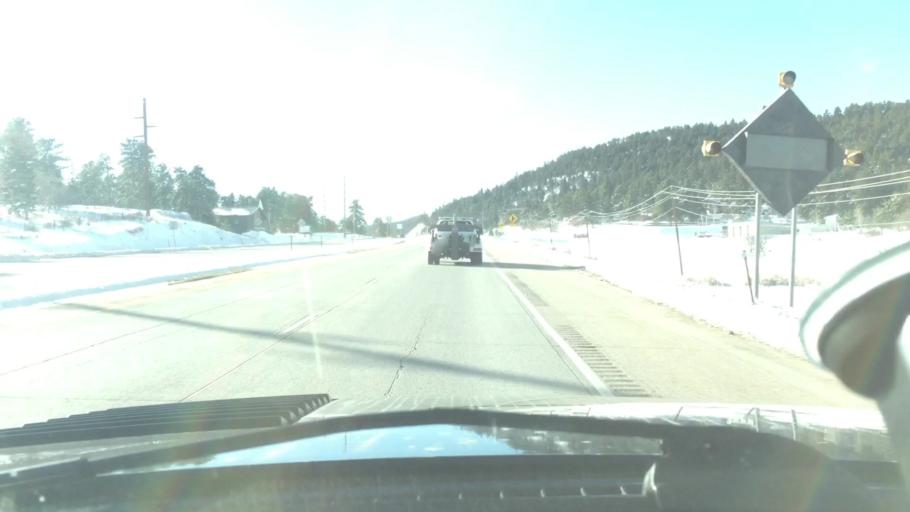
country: US
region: Colorado
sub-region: Jefferson County
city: Indian Hills
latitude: 39.5664
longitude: -105.2387
